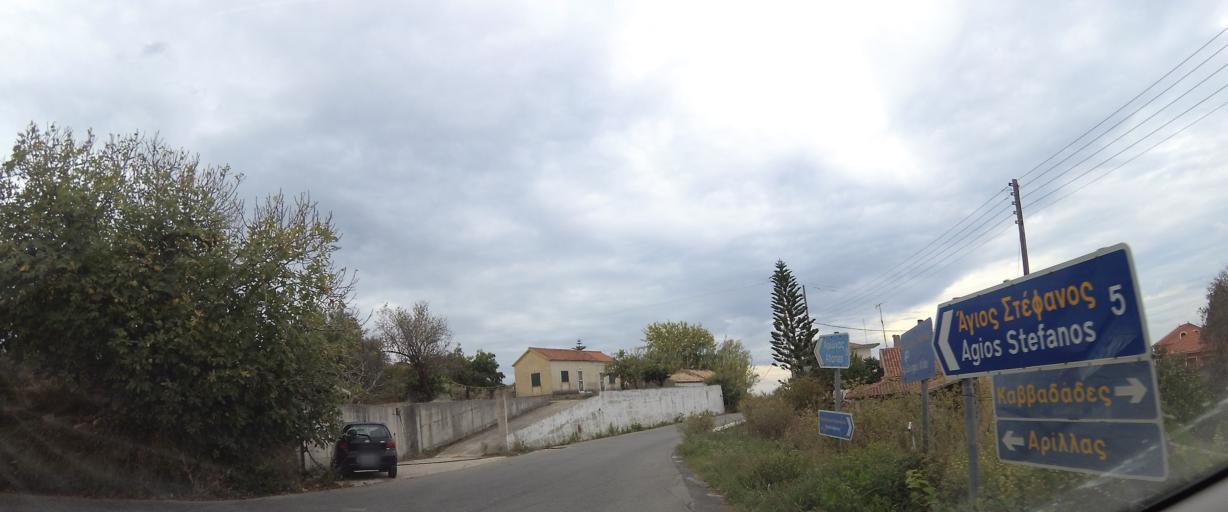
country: GR
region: Ionian Islands
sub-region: Nomos Kerkyras
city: Agios Georgis
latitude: 39.7401
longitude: 19.6762
